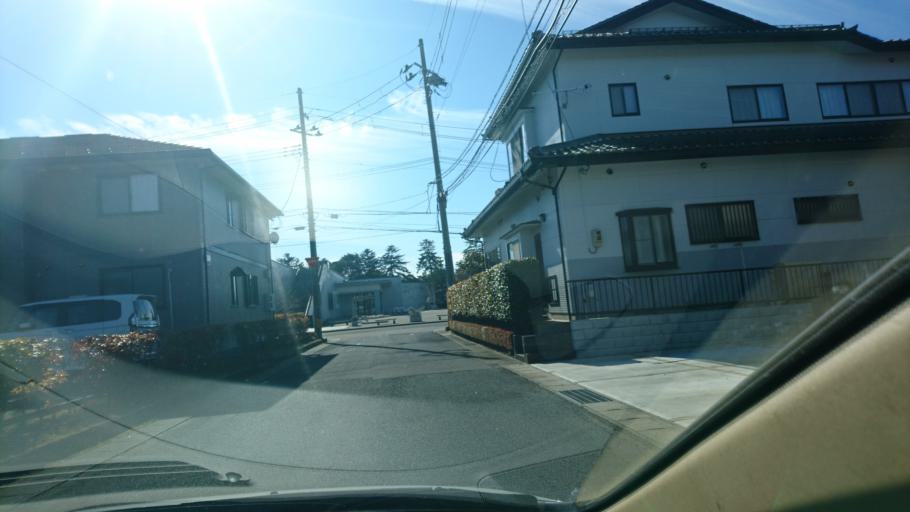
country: JP
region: Miyagi
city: Furukawa
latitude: 38.5824
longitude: 140.9735
